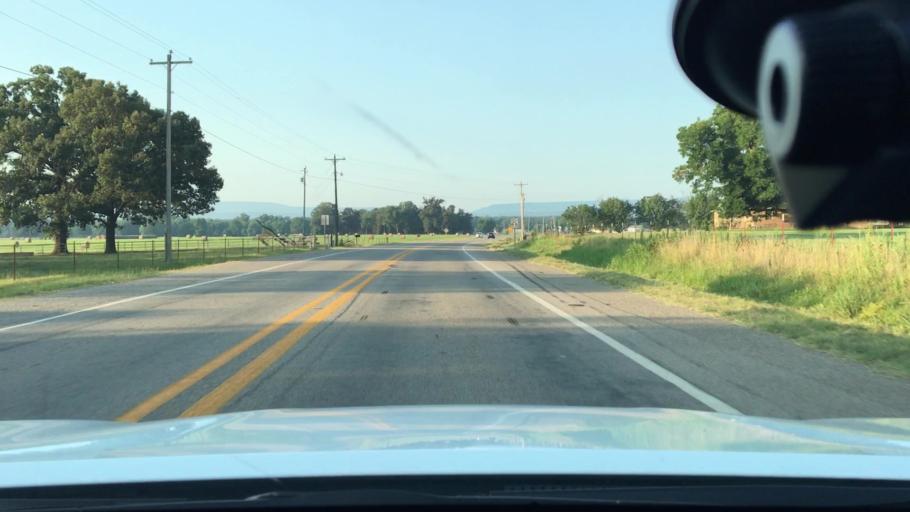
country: US
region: Arkansas
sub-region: Johnson County
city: Clarksville
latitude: 35.3836
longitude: -93.5296
